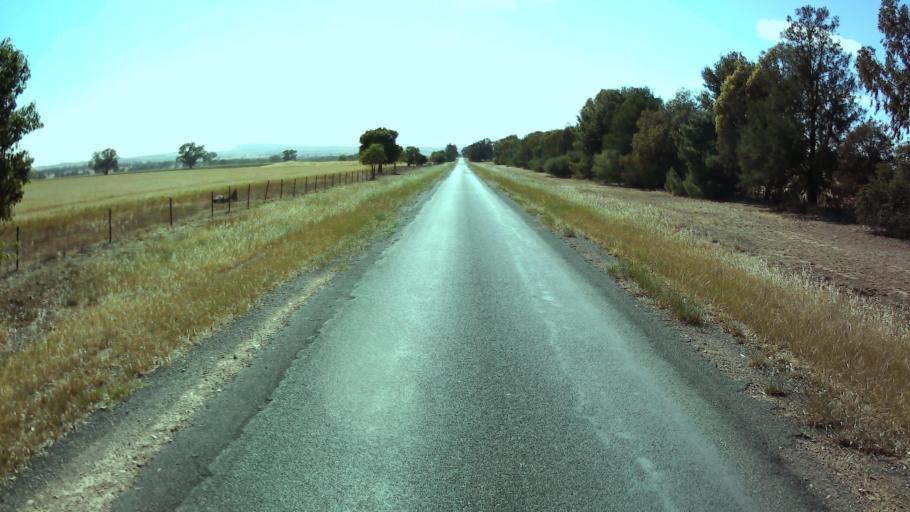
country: AU
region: New South Wales
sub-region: Weddin
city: Grenfell
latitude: -34.0625
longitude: 148.2808
